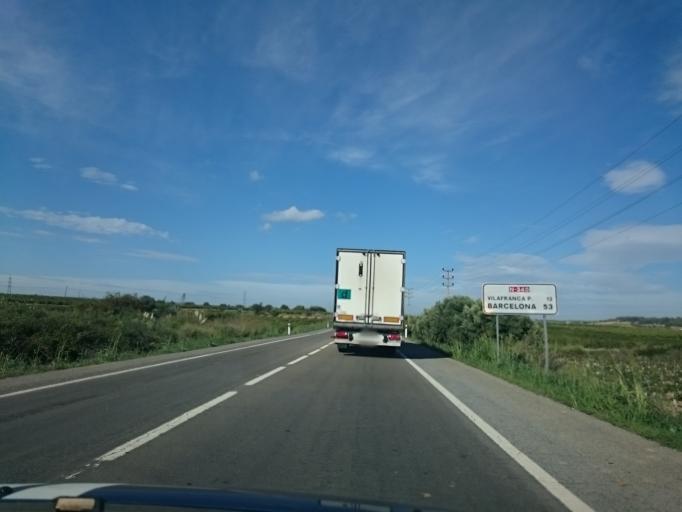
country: ES
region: Catalonia
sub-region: Provincia de Barcelona
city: Castellet
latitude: 41.2721
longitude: 1.6090
